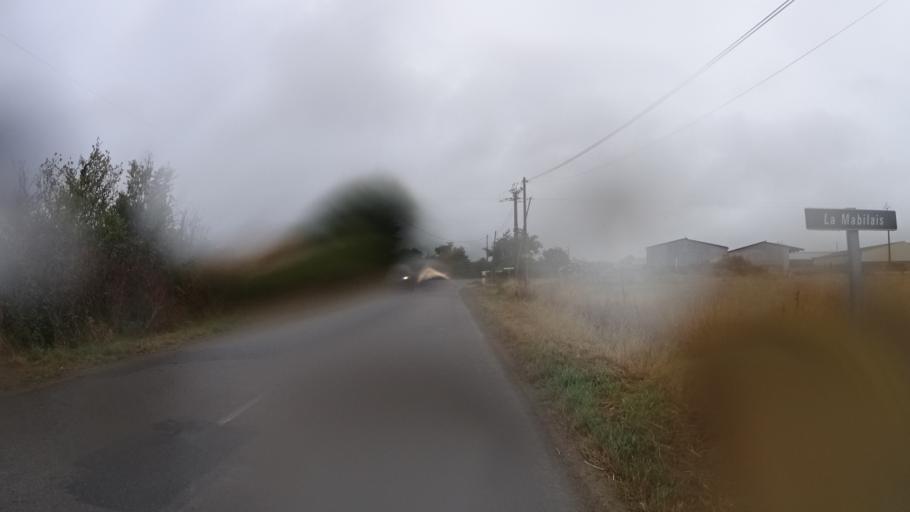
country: FR
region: Pays de la Loire
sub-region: Departement de la Loire-Atlantique
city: Corsept
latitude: 47.2716
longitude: -2.0895
